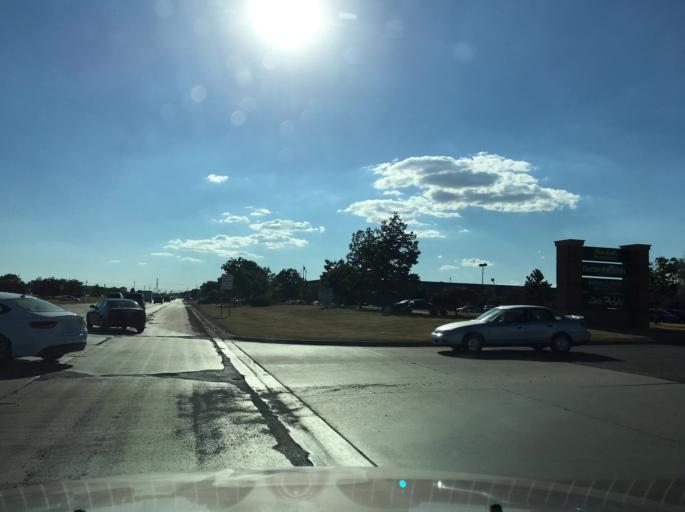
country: US
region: Michigan
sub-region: Macomb County
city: Utica
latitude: 42.6277
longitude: -82.9854
